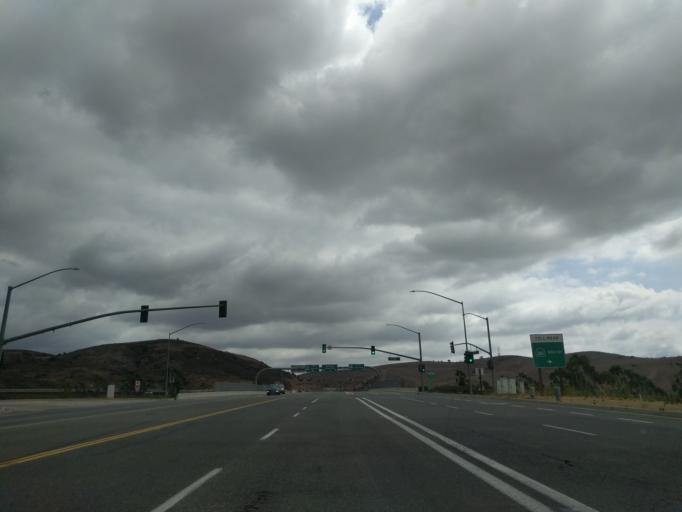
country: US
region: California
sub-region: Orange County
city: North Tustin
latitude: 33.7834
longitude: -117.7502
